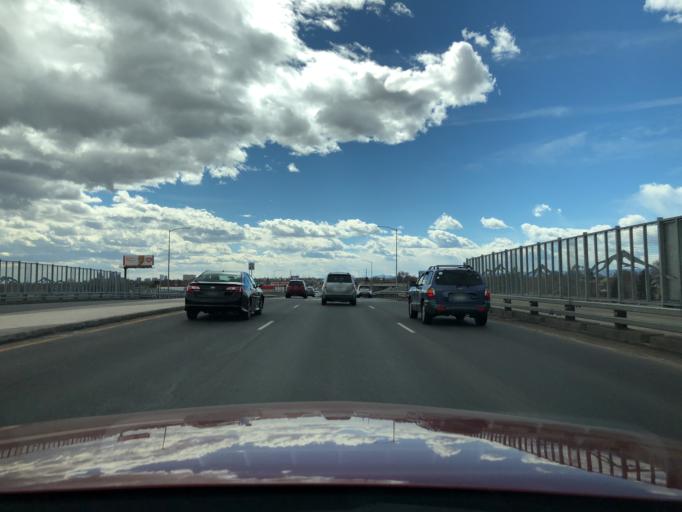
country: US
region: Colorado
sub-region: Adams County
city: Berkley
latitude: 39.8213
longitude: -105.0251
